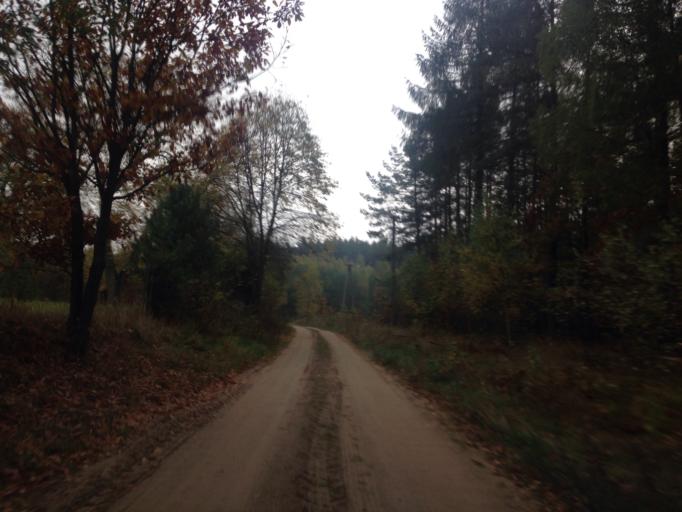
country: PL
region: Warmian-Masurian Voivodeship
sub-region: Powiat dzialdowski
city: Lidzbark
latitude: 53.2724
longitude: 19.7237
